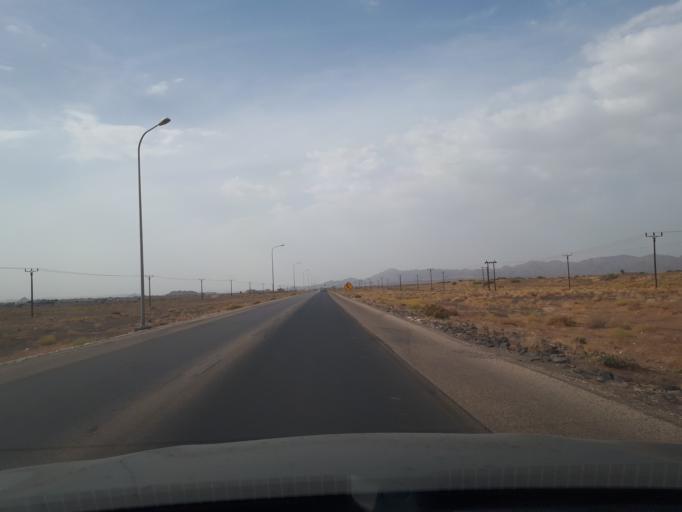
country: OM
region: Ash Sharqiyah
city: Al Qabil
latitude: 22.5203
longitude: 58.7363
